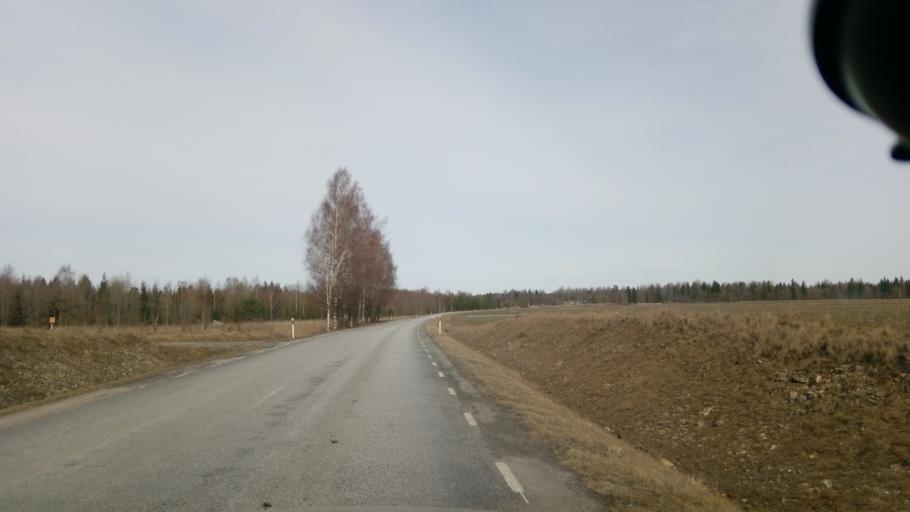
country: EE
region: Raplamaa
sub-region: Rapla vald
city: Rapla
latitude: 59.0338
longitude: 24.8356
